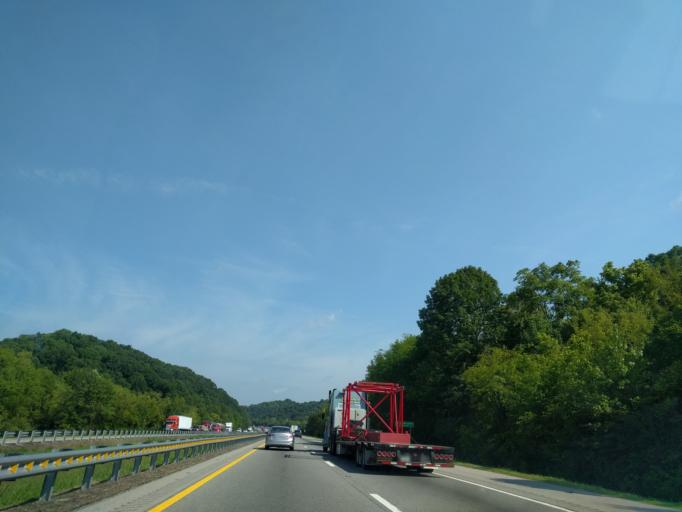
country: US
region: Tennessee
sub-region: Sumner County
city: Millersville
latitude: 36.3911
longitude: -86.7158
